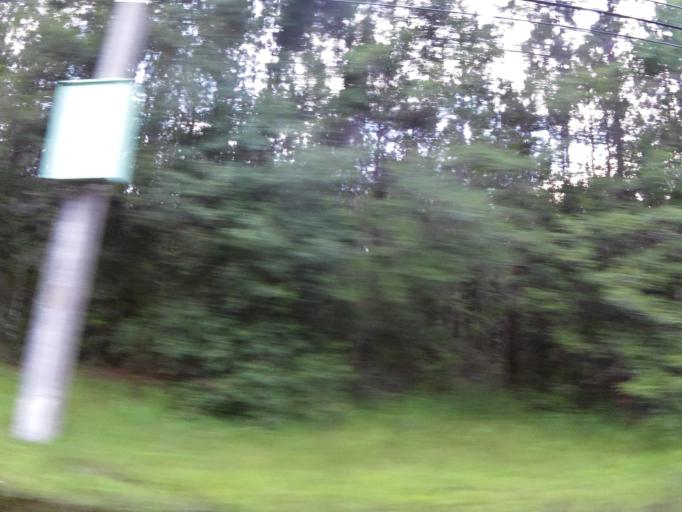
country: US
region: Florida
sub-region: Duval County
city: Jacksonville
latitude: 30.3549
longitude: -81.7732
